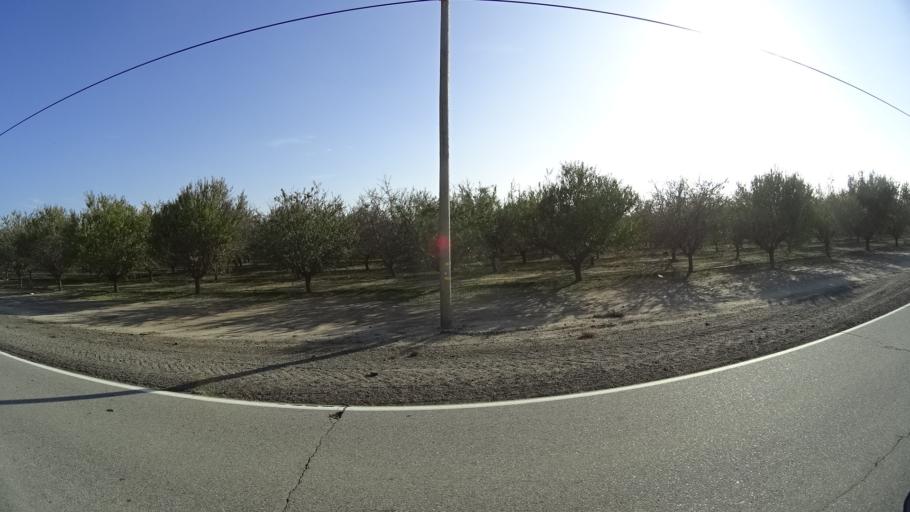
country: US
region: California
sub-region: Kern County
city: Rosedale
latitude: 35.2962
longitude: -119.1799
